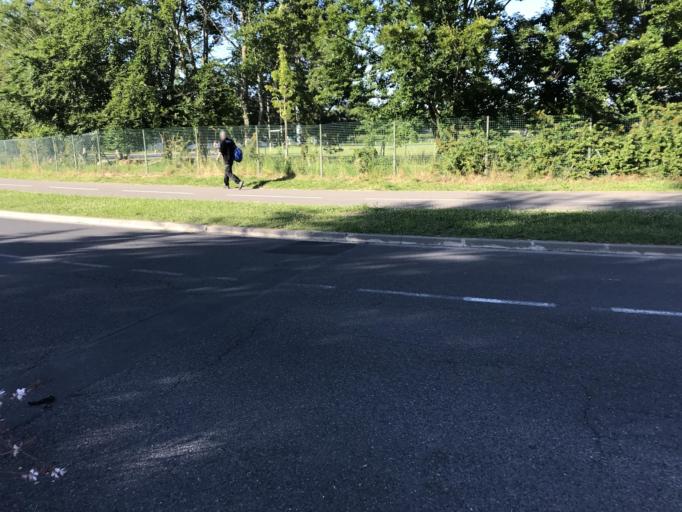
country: FR
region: Ile-de-France
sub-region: Departement de l'Essonne
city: Nozay
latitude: 48.6638
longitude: 2.2352
